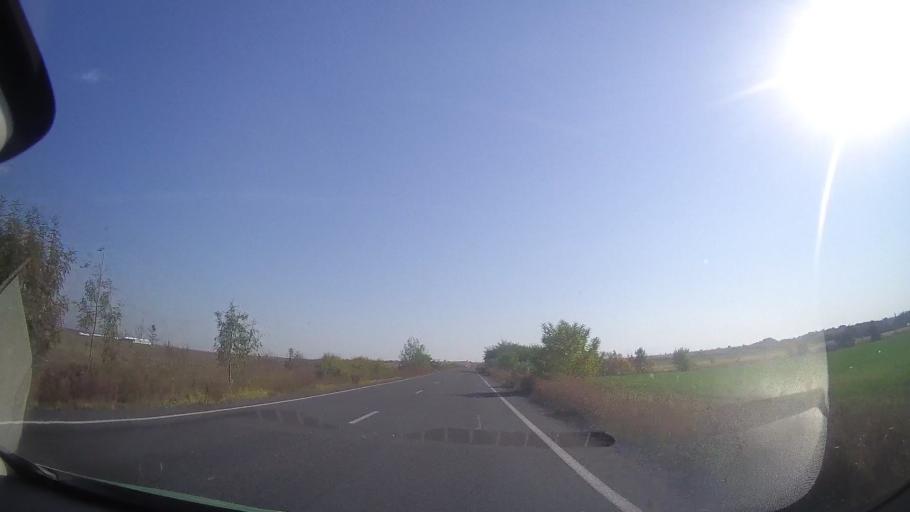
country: RO
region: Timis
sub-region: Comuna Topolovatu Mare
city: Topolovatu Mare
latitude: 45.7755
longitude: 21.6479
